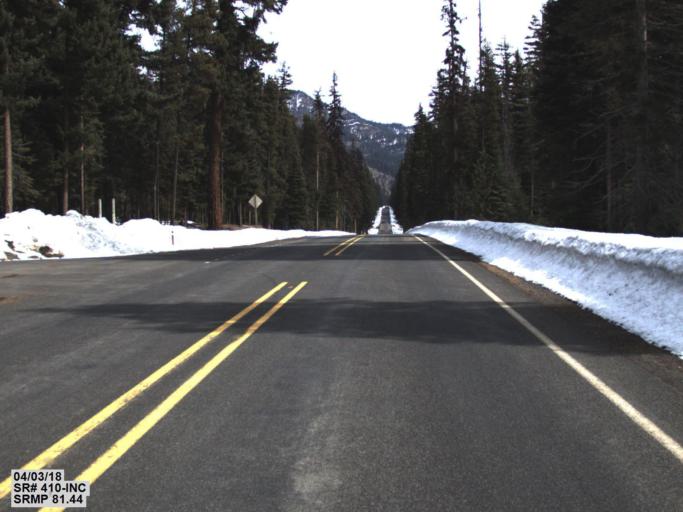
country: US
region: Washington
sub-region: Kittitas County
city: Cle Elum
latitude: 46.9521
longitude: -121.3057
